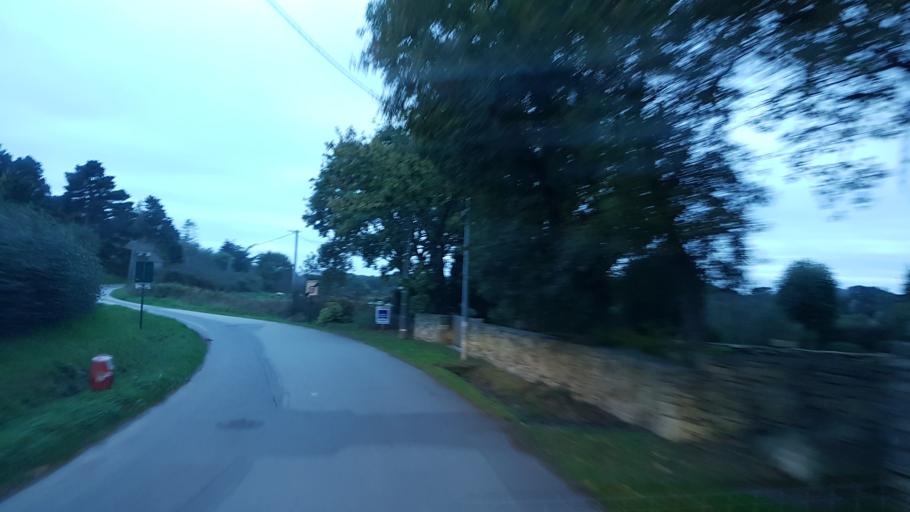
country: FR
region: Brittany
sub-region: Departement du Morbihan
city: Sarzeau
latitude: 47.5390
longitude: -2.7948
